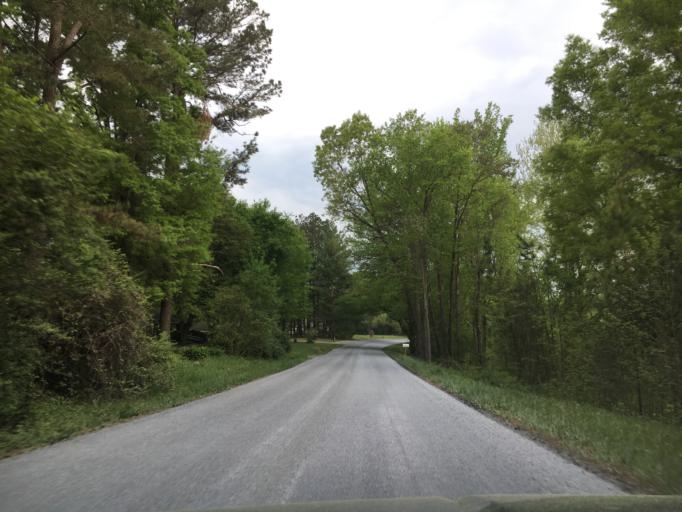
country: US
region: Virginia
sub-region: Campbell County
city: Brookneal
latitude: 36.9416
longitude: -78.9504
